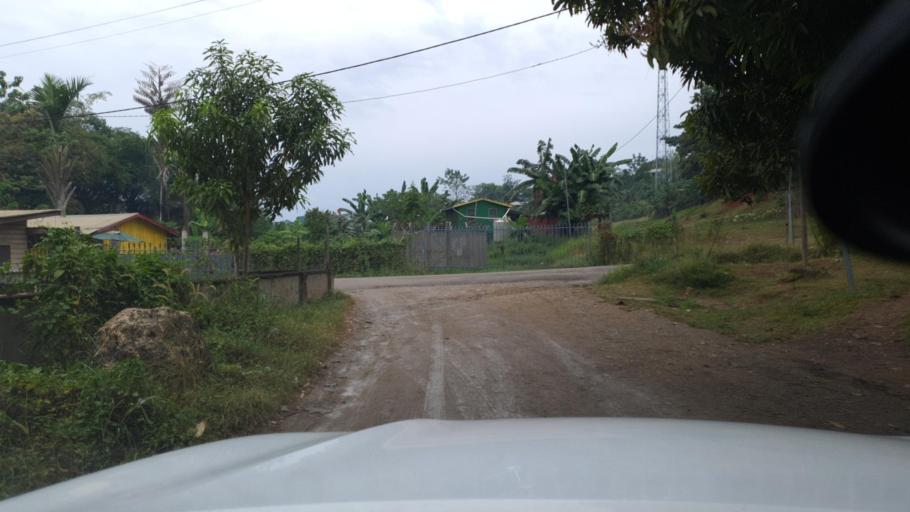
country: SB
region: Guadalcanal
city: Honiara
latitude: -9.4472
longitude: 159.9799
